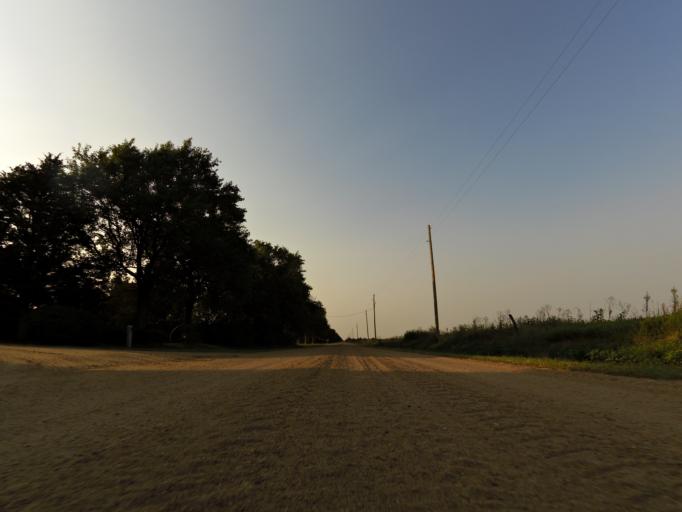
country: US
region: Kansas
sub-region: Reno County
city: South Hutchinson
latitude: 37.9864
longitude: -97.9957
